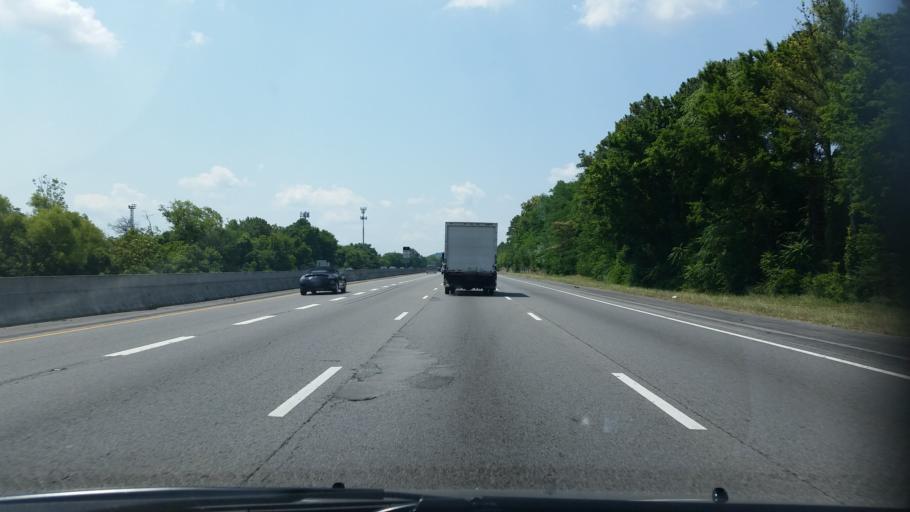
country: US
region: Tennessee
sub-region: Davidson County
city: Oak Hill
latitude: 36.0653
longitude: -86.7713
